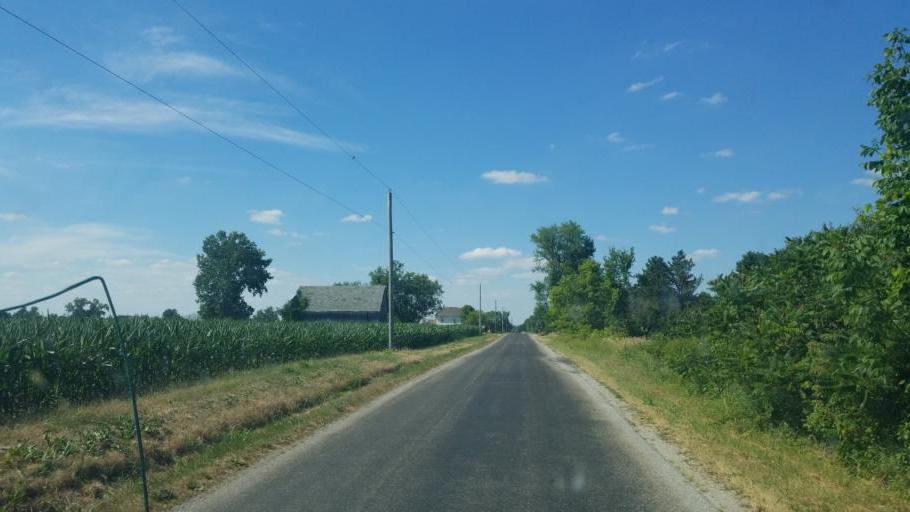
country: US
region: Ohio
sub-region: Defiance County
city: Hicksville
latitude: 41.3615
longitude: -84.7863
